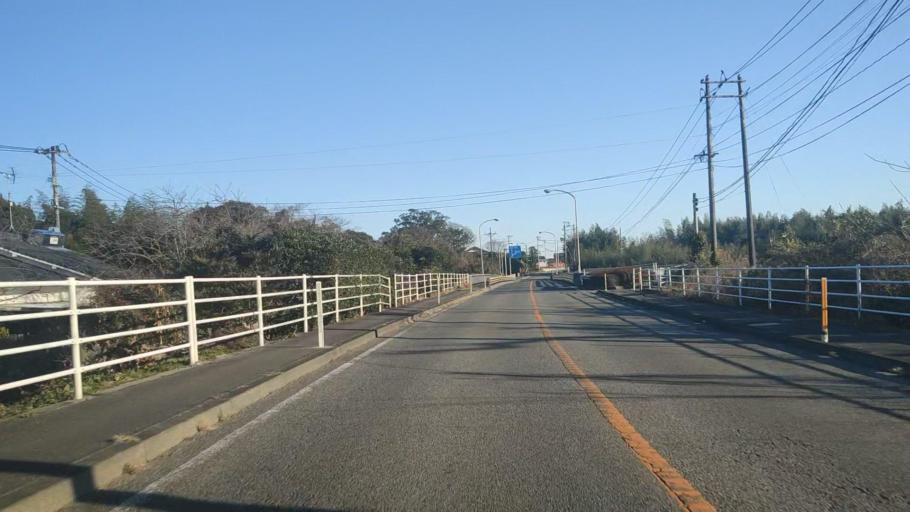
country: JP
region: Miyazaki
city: Takanabe
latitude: 32.2401
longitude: 131.5484
